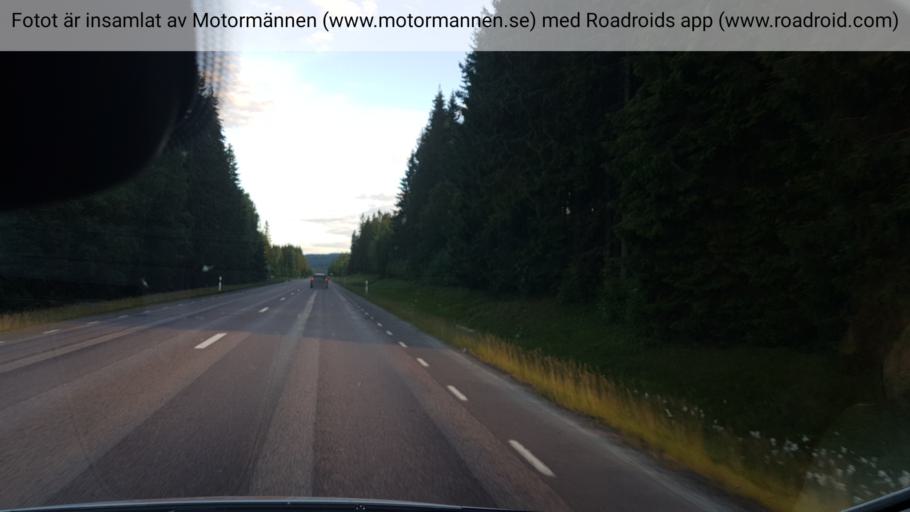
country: SE
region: Vaermland
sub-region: Torsby Kommun
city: Torsby
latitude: 60.1093
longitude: 13.0188
